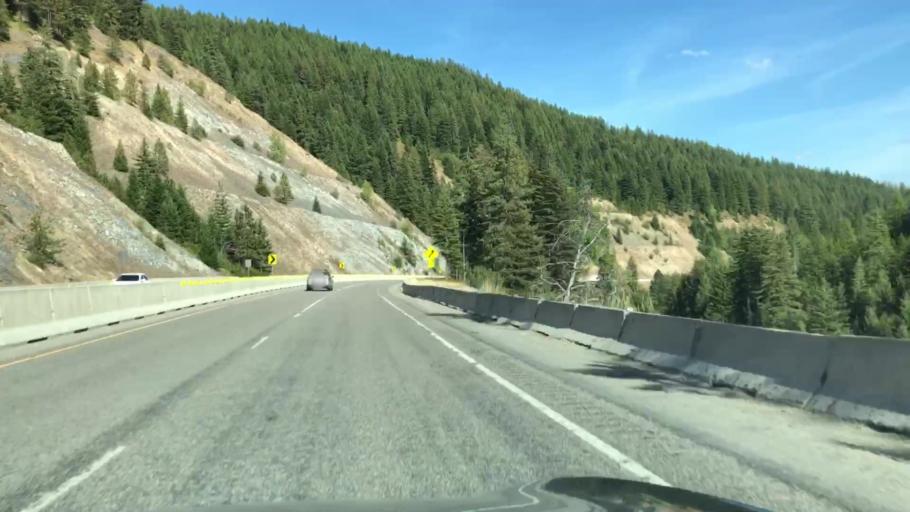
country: US
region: Montana
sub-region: Sanders County
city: Thompson Falls
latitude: 47.4011
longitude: -115.4688
